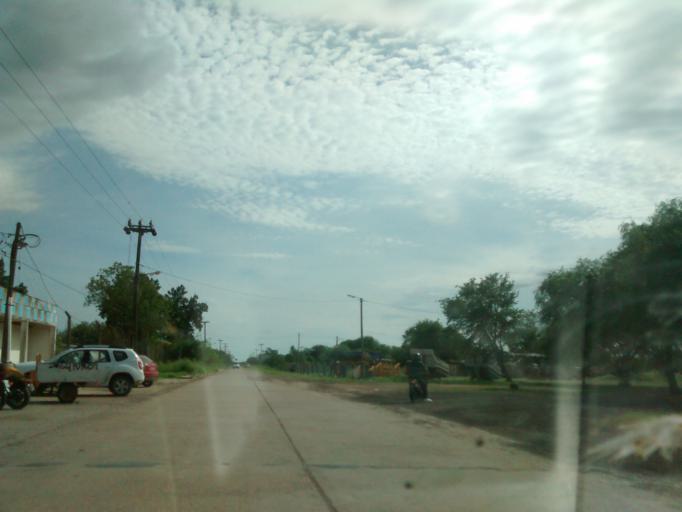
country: AR
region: Chaco
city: Resistencia
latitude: -27.4148
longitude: -58.9666
